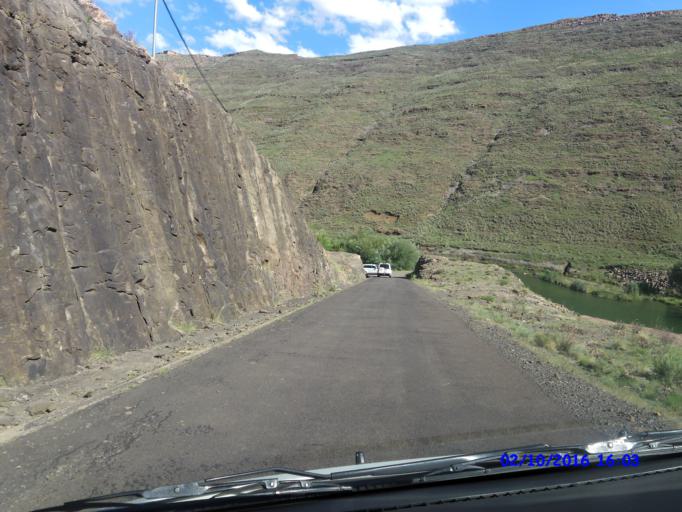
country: LS
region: Maseru
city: Nako
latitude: -29.4581
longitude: 28.0997
